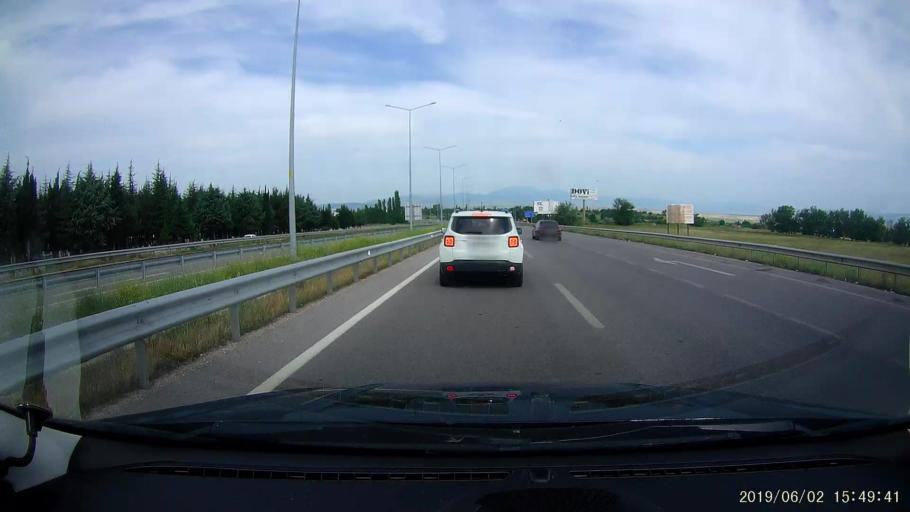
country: TR
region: Amasya
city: Merzifon
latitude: 40.8574
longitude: 35.4667
